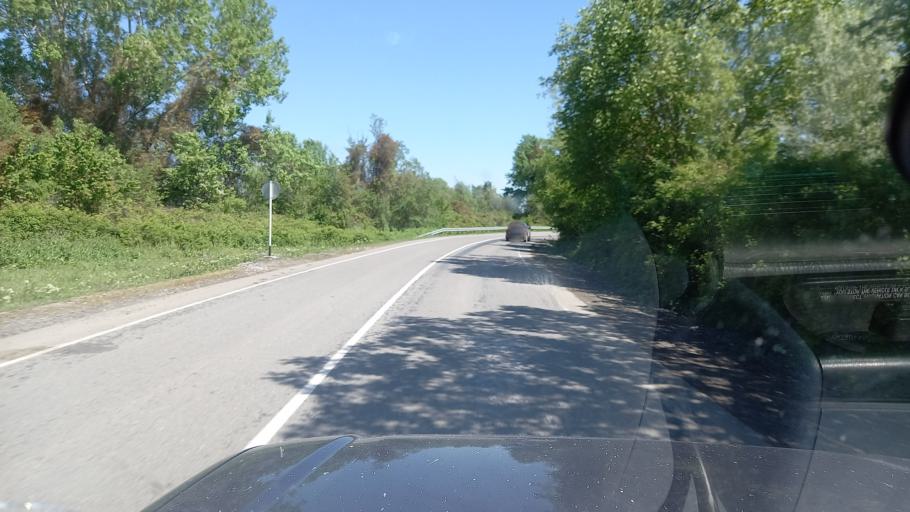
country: RU
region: Dagestan
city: Samur
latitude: 41.7342
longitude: 48.4692
